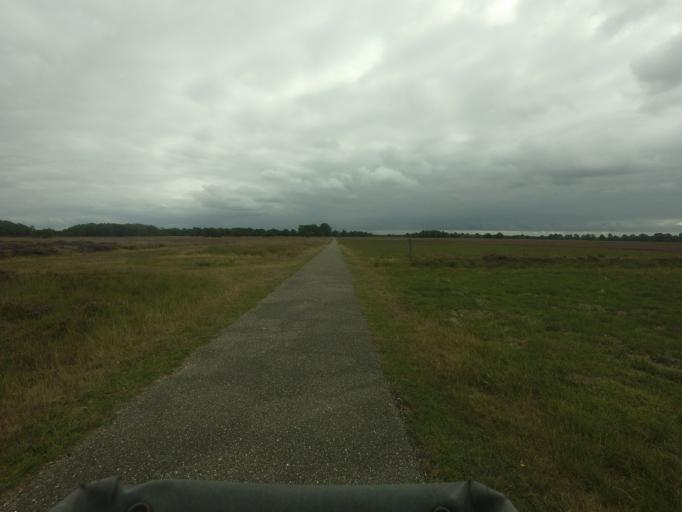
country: NL
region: Friesland
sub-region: Gemeente Weststellingwerf
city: Noordwolde
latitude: 52.9028
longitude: 6.2641
